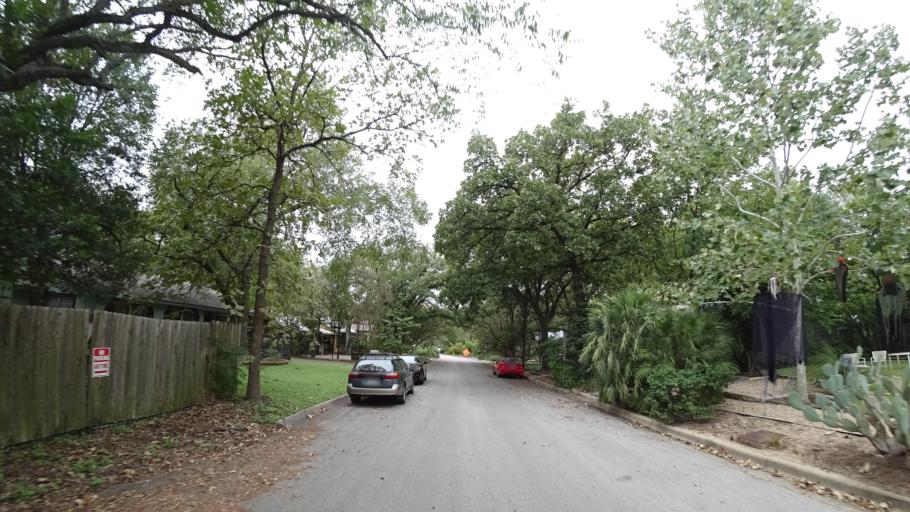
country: US
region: Texas
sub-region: Travis County
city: Austin
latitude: 30.3049
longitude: -97.7218
